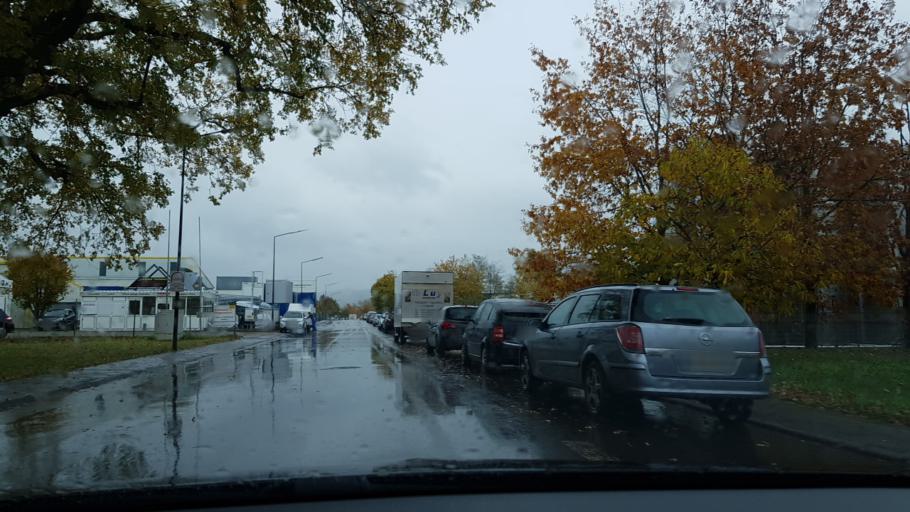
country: DE
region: Rheinland-Pfalz
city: Neuerburg
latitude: 49.9793
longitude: 6.9498
